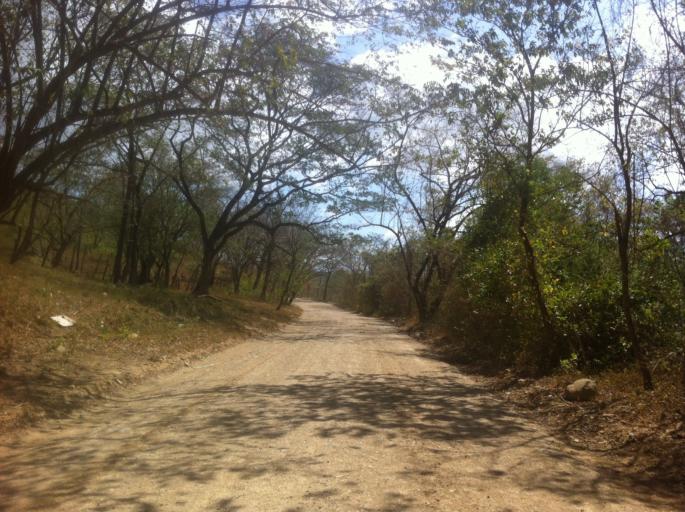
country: NI
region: Rivas
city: Tola
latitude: 11.4103
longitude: -86.0084
